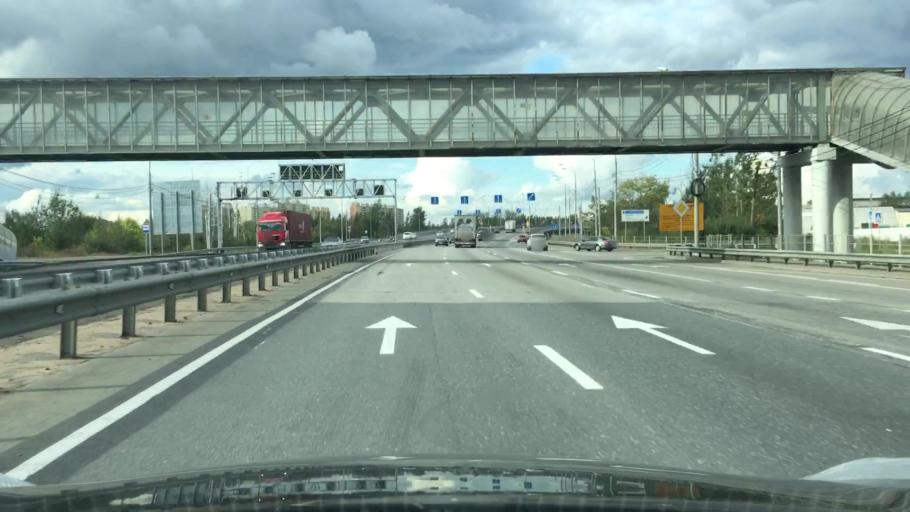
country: RU
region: Tverskaya
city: Tver
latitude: 56.8378
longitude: 35.7951
